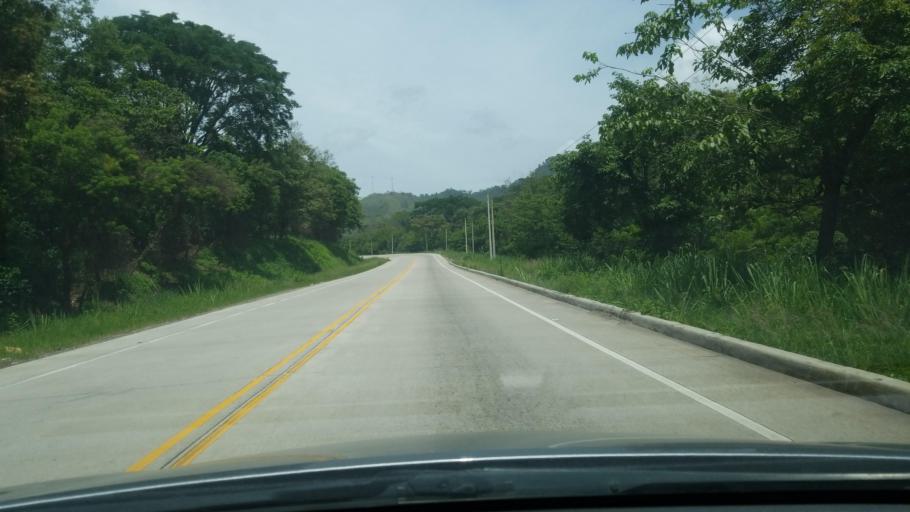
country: HN
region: Copan
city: Agua Caliente
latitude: 14.8729
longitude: -88.7795
